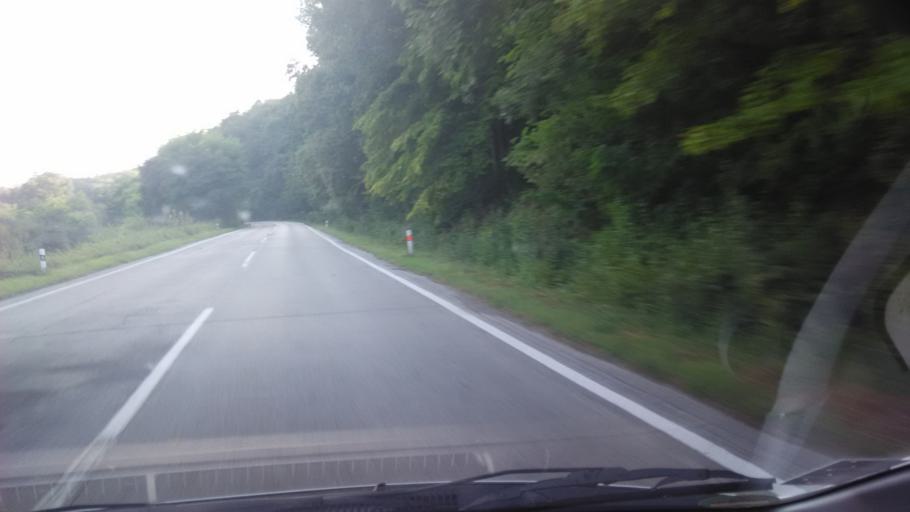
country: SK
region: Nitriansky
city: Zlate Moravce
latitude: 48.4445
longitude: 18.4115
